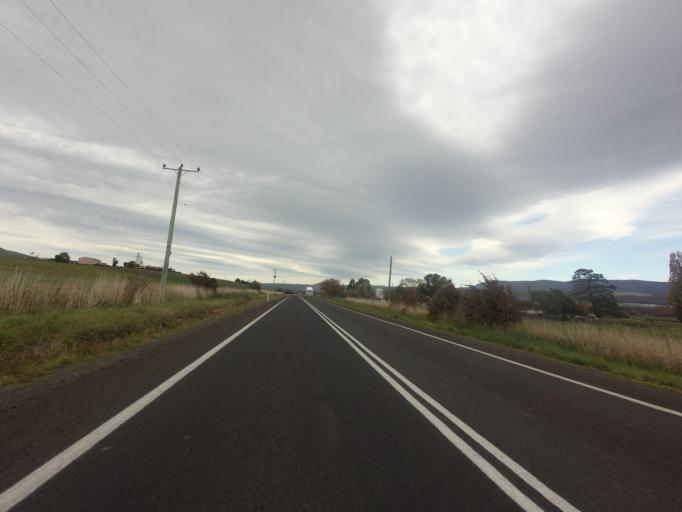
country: AU
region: Tasmania
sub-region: Derwent Valley
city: New Norfolk
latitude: -42.4943
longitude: 146.7291
